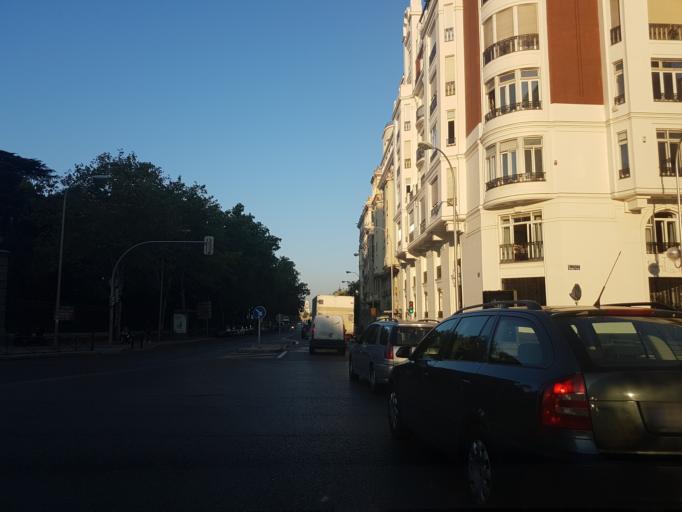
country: ES
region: Madrid
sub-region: Provincia de Madrid
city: Salamanca
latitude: 40.4217
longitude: -3.6799
